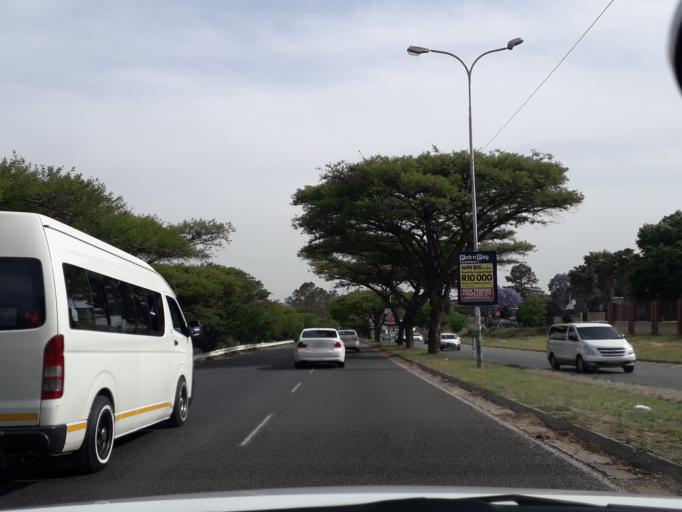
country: ZA
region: Gauteng
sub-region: City of Johannesburg Metropolitan Municipality
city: Johannesburg
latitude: -26.0771
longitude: 28.0261
